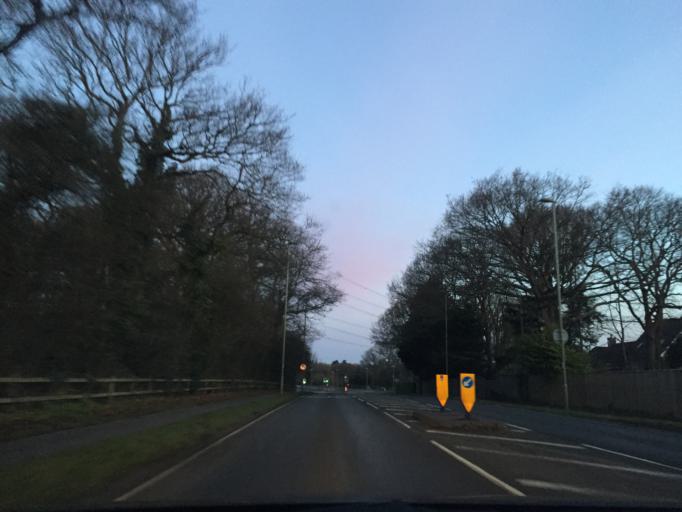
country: GB
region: England
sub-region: Hampshire
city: Botley
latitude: 50.8596
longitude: -1.2500
